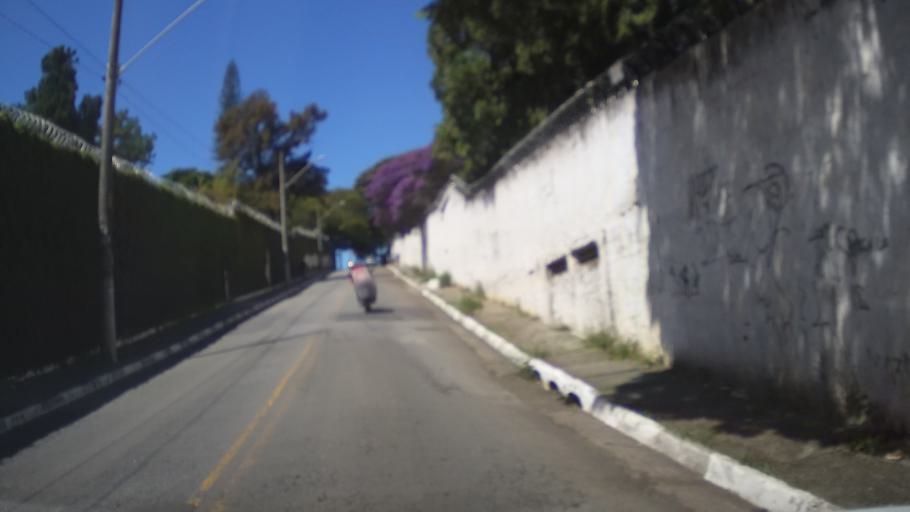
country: BR
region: Sao Paulo
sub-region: Guarulhos
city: Guarulhos
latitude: -23.4546
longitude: -46.5425
